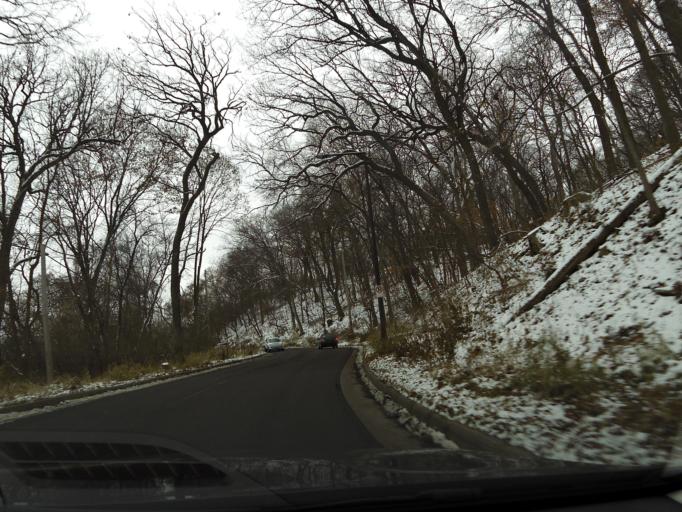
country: US
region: Minnesota
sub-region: Dakota County
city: Mendota Heights
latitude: 44.9060
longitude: -93.1625
